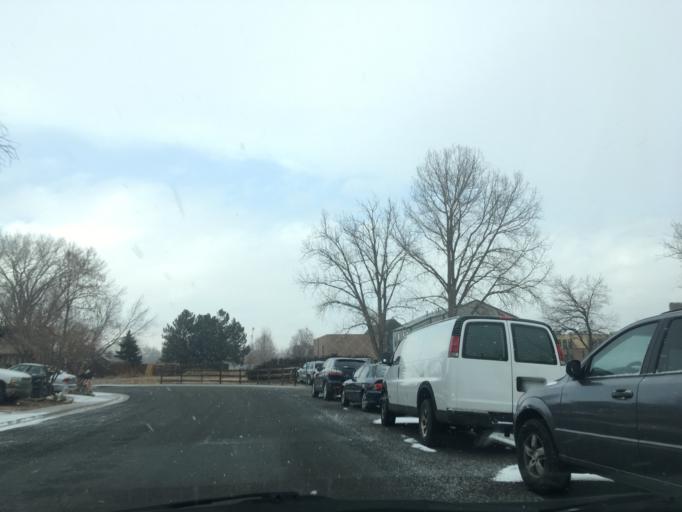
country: US
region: Colorado
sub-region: Boulder County
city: Lafayette
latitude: 39.9894
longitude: -105.0792
